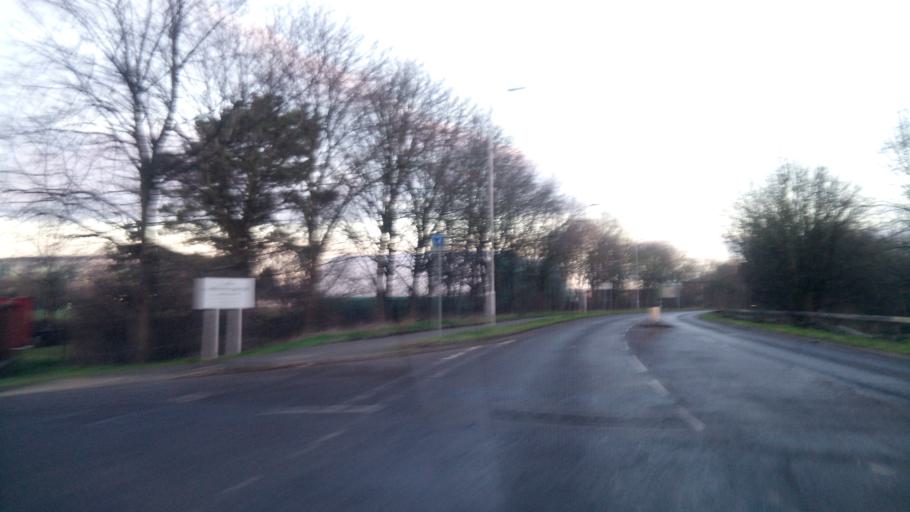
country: GB
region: England
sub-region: Peterborough
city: Peterborough
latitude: 52.5838
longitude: -0.2720
